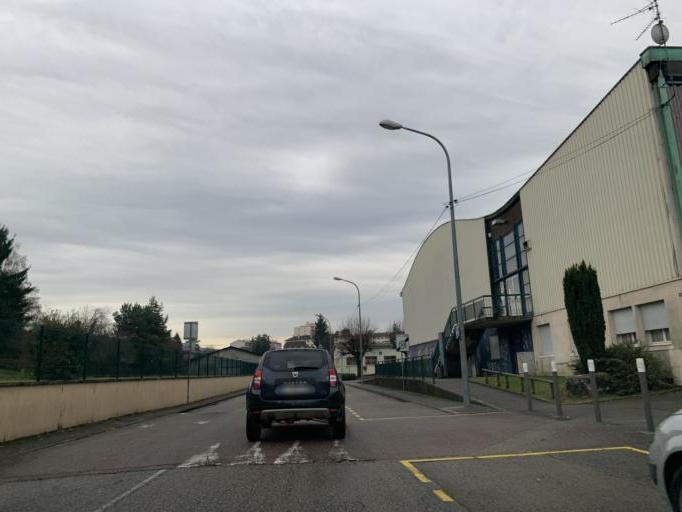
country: FR
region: Rhone-Alpes
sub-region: Departement de l'Ain
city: Belley
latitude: 45.7627
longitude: 5.6916
